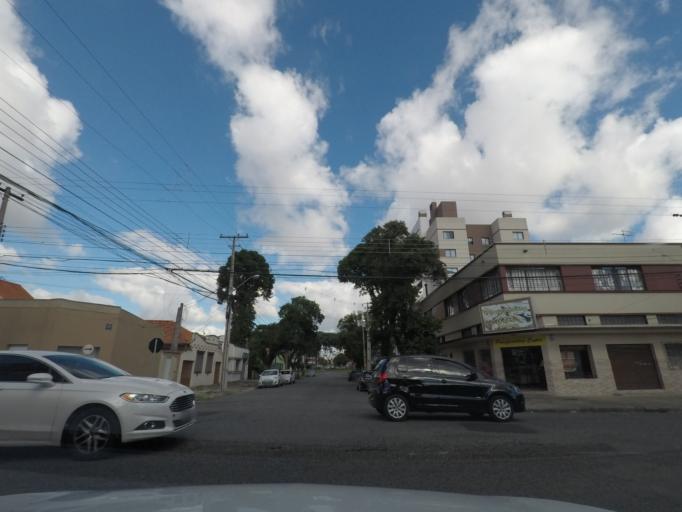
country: BR
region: Parana
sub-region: Curitiba
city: Curitiba
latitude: -25.4442
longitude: -49.2576
